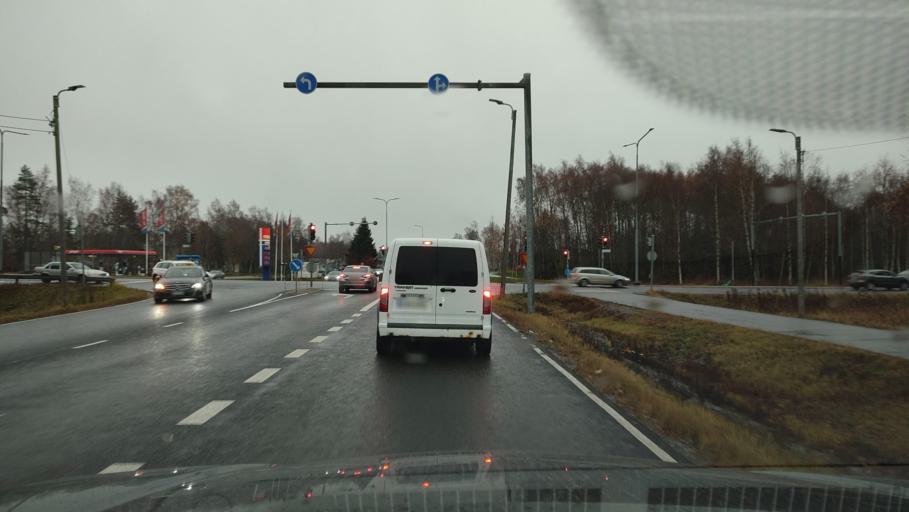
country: FI
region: Ostrobothnia
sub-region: Vaasa
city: Korsholm
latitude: 63.0902
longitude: 21.6546
